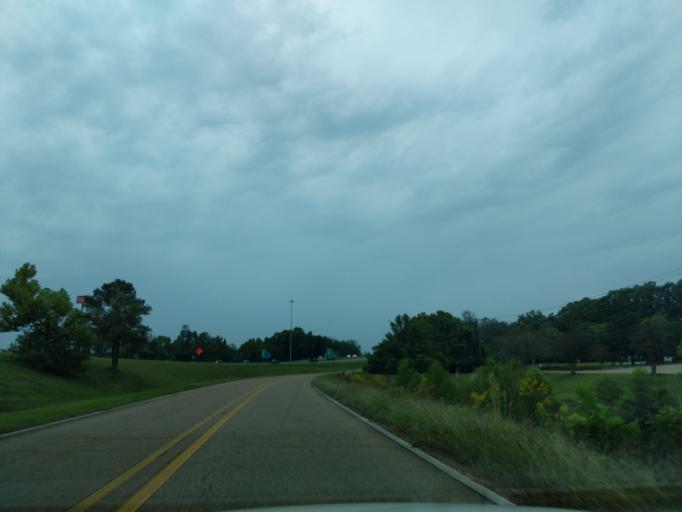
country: US
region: Mississippi
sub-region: Warren County
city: Vicksburg
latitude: 32.3189
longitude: -90.8803
